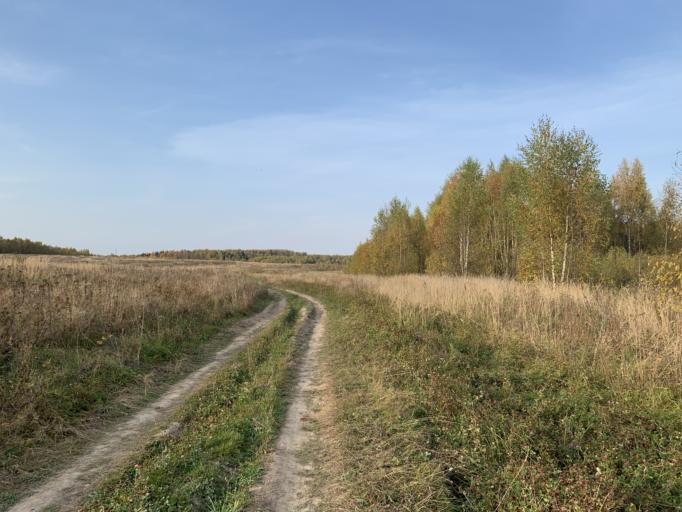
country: RU
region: Jaroslavl
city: Porech'ye-Rybnoye
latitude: 56.9824
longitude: 39.3842
